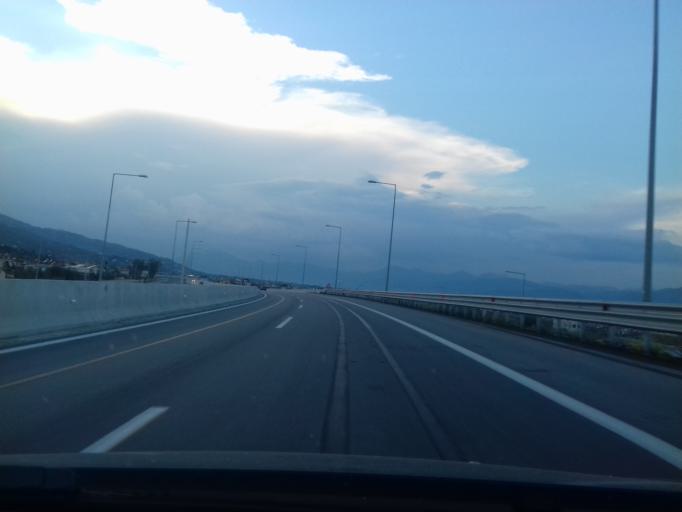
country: GR
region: West Greece
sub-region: Nomos Achaias
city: Aigio
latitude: 38.2626
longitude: 22.0591
